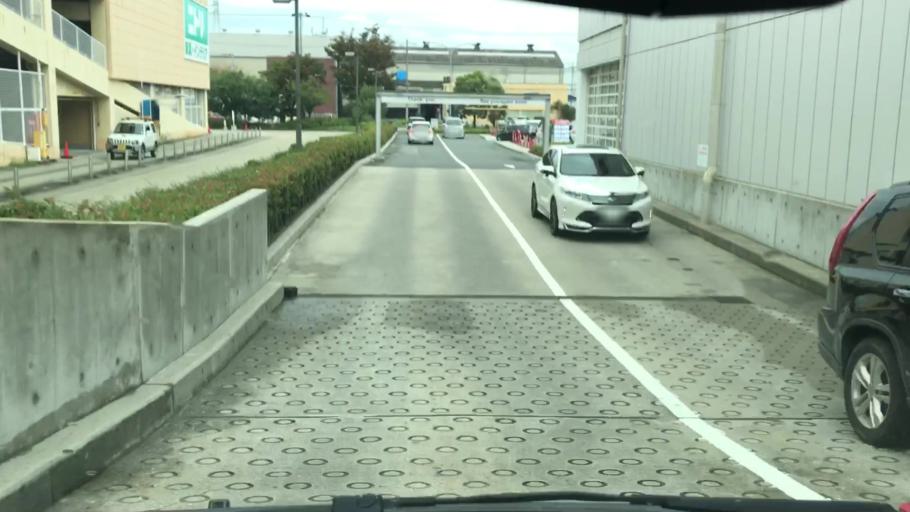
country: JP
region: Hyogo
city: Amagasaki
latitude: 34.7417
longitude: 135.4433
